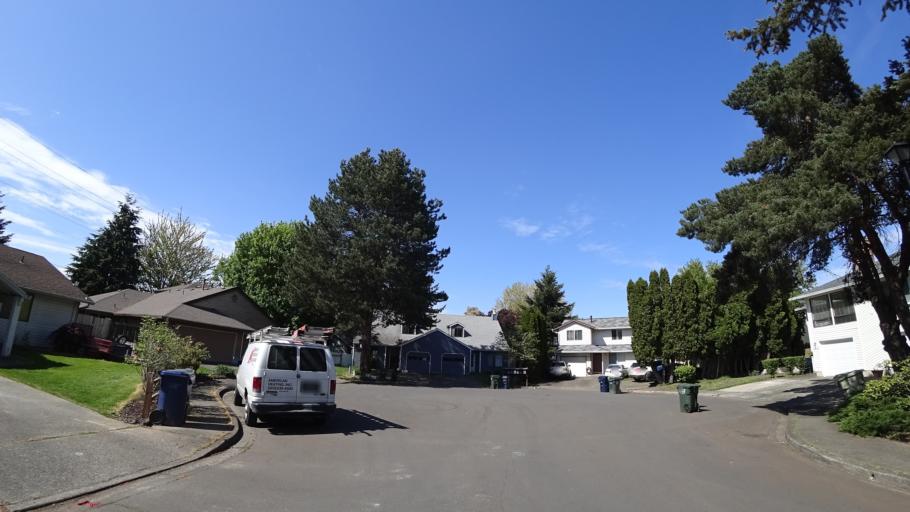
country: US
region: Oregon
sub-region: Washington County
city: Aloha
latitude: 45.5013
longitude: -122.9015
